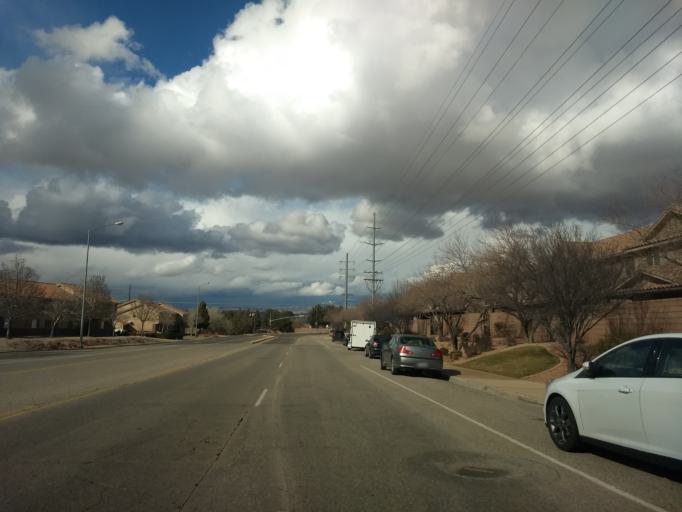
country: US
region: Utah
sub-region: Washington County
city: Saint George
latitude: 37.0499
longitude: -113.5554
